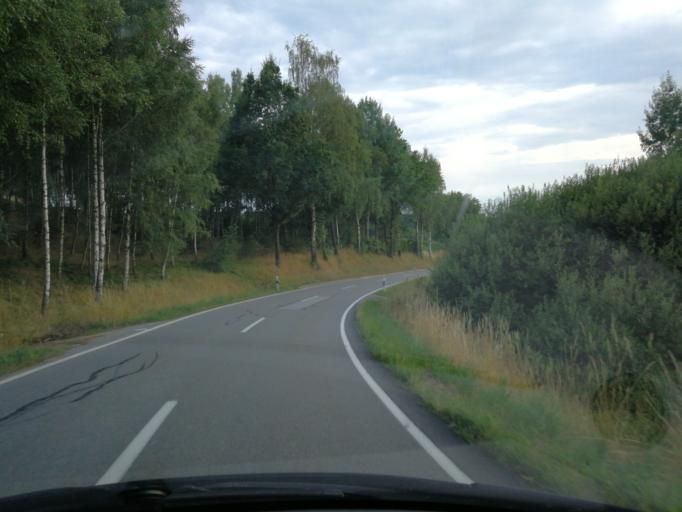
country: DE
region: Bavaria
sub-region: Lower Bavaria
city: Haibach
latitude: 49.0340
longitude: 12.7219
